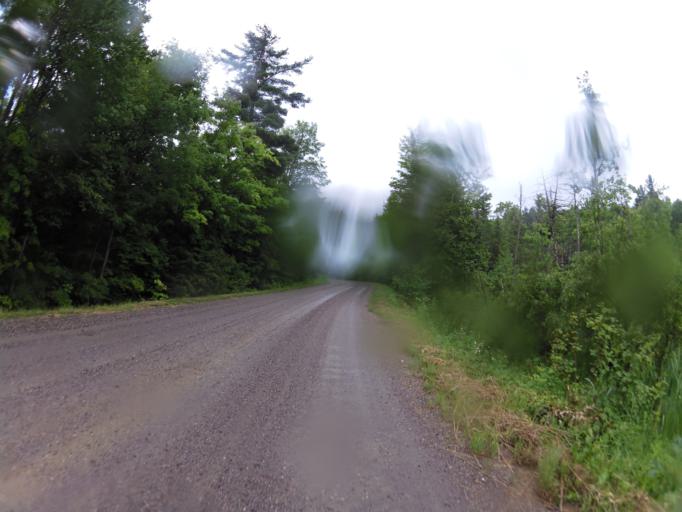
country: CA
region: Ontario
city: Perth
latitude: 45.0790
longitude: -76.5877
